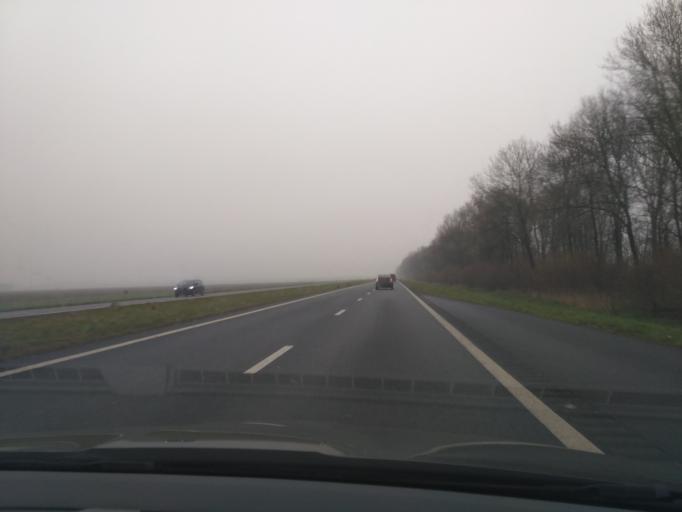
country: NL
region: Flevoland
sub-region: Gemeente Zeewolde
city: Zeewolde
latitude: 52.3663
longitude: 5.5304
